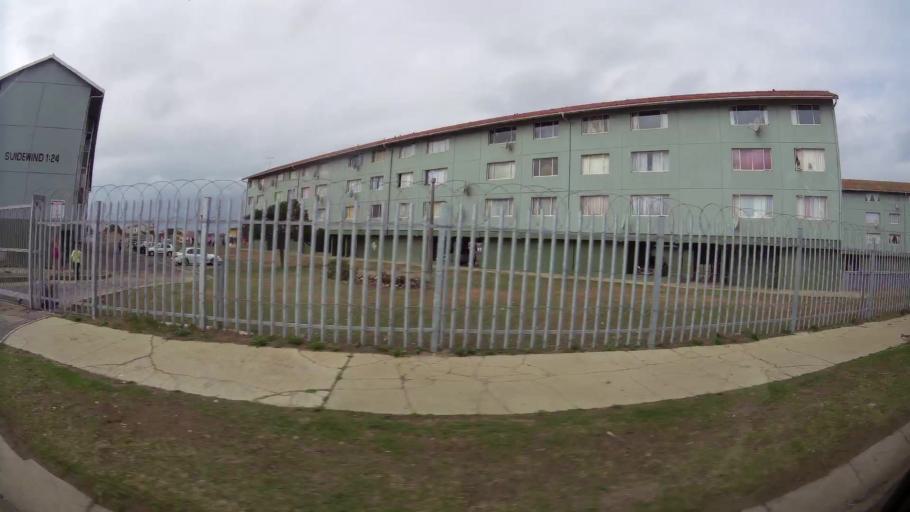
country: ZA
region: Eastern Cape
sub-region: Nelson Mandela Bay Metropolitan Municipality
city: Port Elizabeth
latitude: -33.8948
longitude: 25.5531
